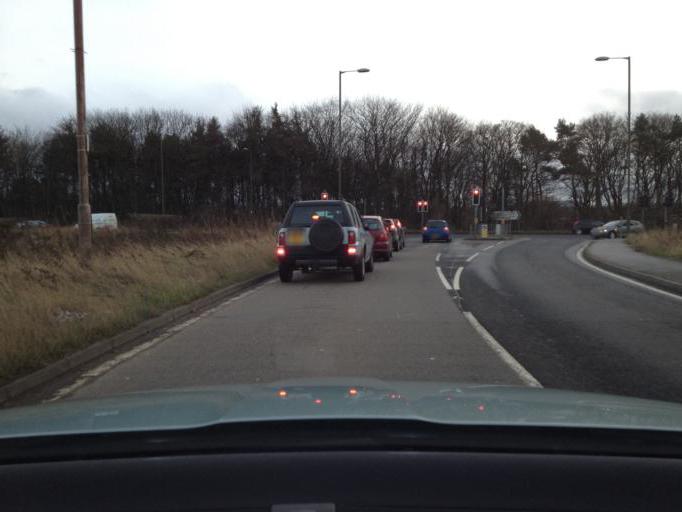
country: GB
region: Scotland
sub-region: Edinburgh
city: Newbridge
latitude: 55.9415
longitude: -3.4122
